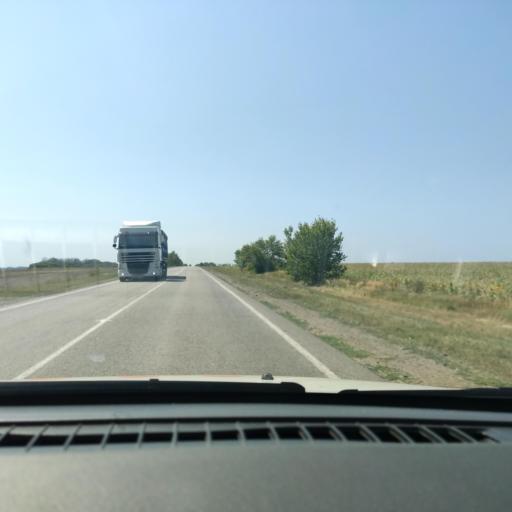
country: RU
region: Voronezj
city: Imeni Pervogo Maya
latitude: 50.6929
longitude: 39.3793
